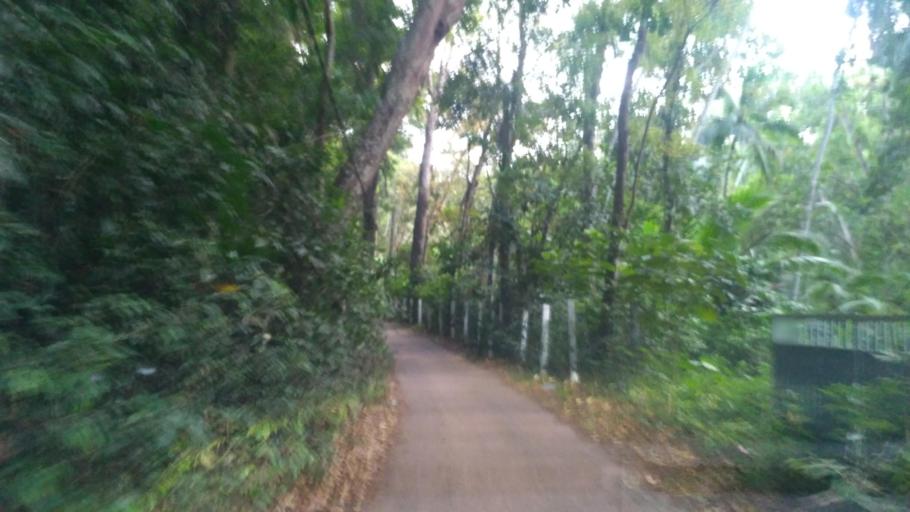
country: LK
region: North Western
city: Kuliyapitiya
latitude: 7.3356
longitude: 80.0044
